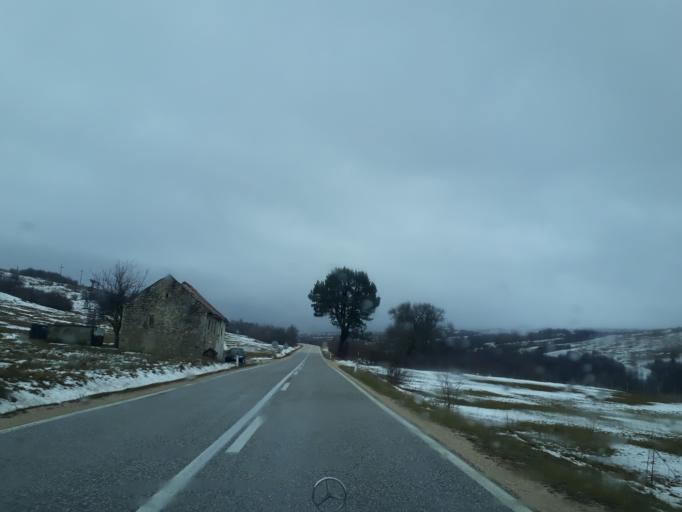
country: BA
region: Federation of Bosnia and Herzegovina
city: Tomislavgrad
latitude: 43.8106
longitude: 17.2037
